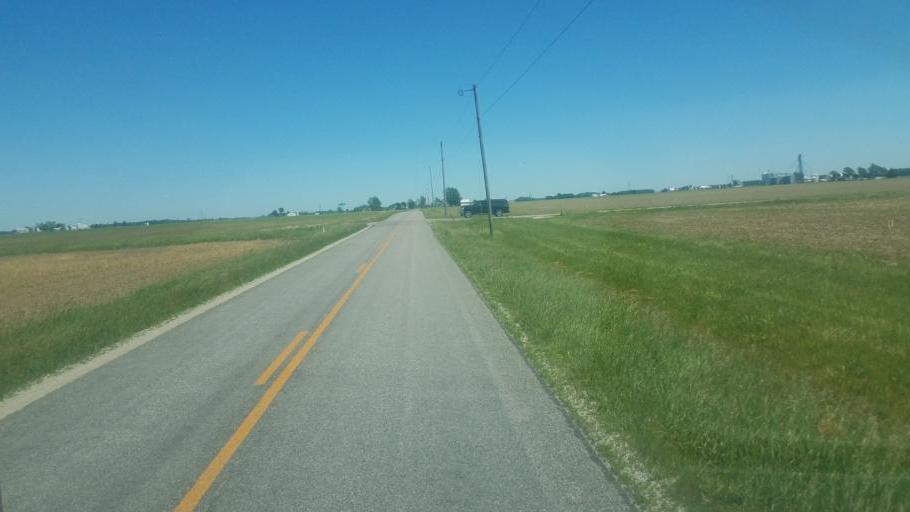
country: US
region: Ohio
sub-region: Shelby County
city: Sidney
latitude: 40.2111
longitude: -84.1159
